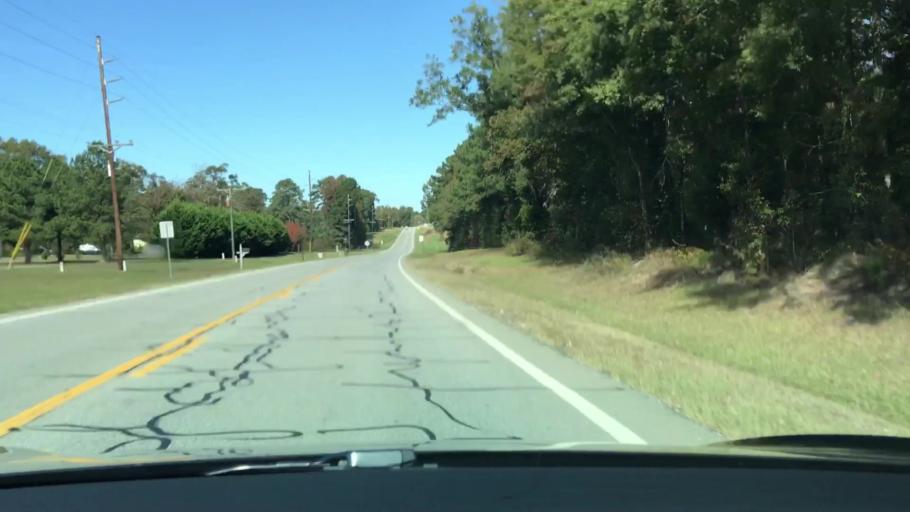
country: US
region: Georgia
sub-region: Warren County
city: Warrenton
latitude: 33.3932
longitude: -82.6491
